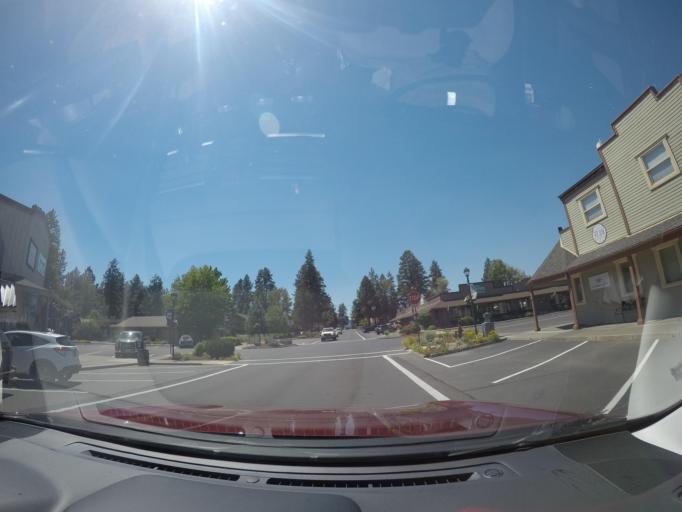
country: US
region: Oregon
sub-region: Deschutes County
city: Sisters
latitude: 44.2905
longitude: -121.5496
